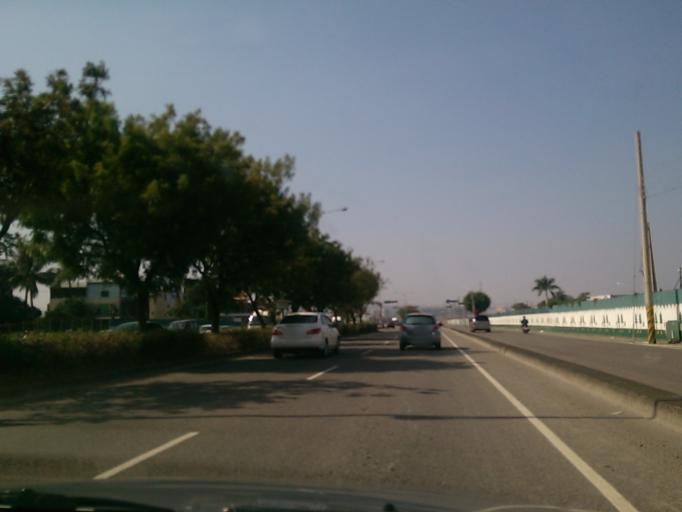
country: TW
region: Taiwan
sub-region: Taichung City
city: Taichung
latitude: 24.1244
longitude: 120.6329
